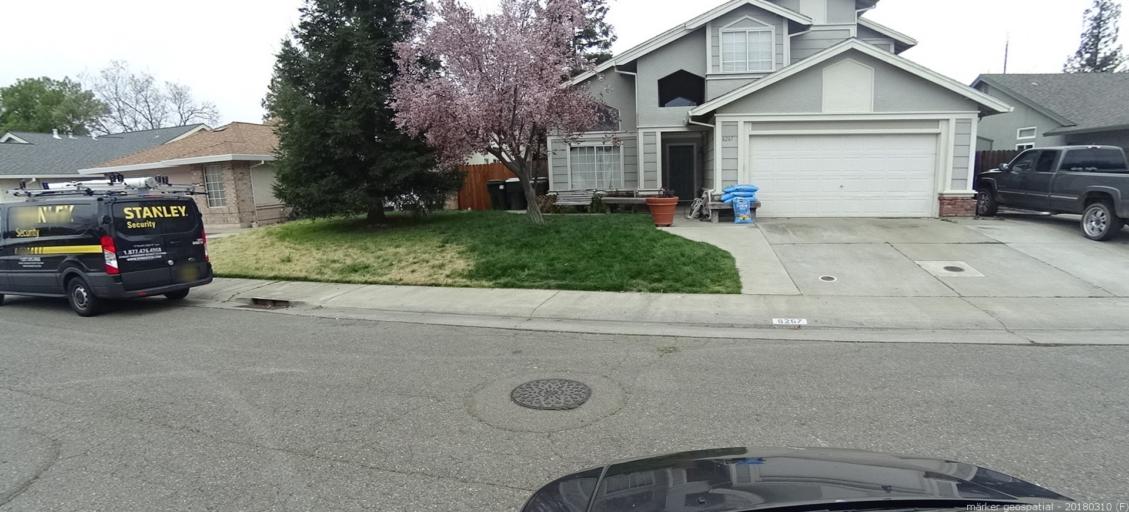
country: US
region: California
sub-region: Sacramento County
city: Vineyard
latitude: 38.4574
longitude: -121.3790
